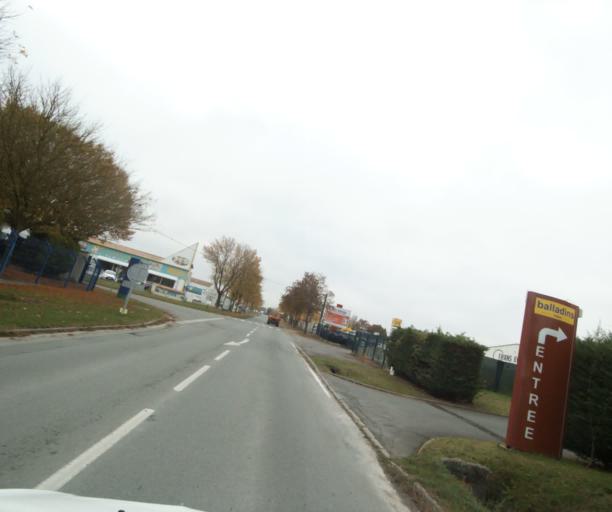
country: FR
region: Poitou-Charentes
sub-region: Departement de la Charente-Maritime
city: Saintes
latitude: 45.7485
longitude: -0.6688
